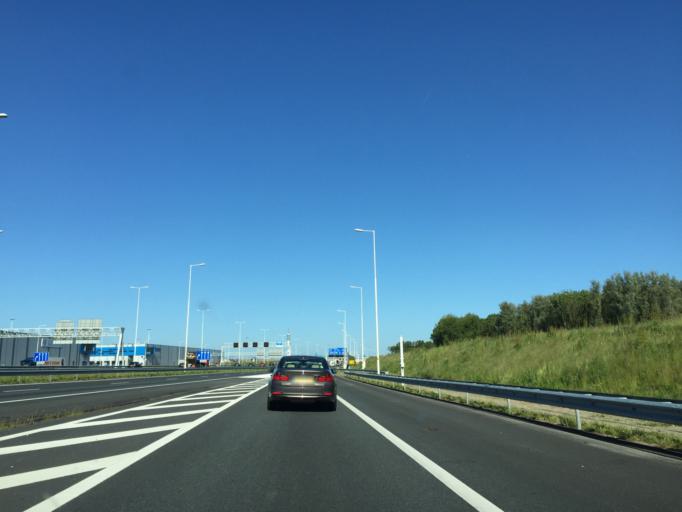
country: NL
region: South Holland
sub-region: Gemeente Albrandswaard
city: Rhoon
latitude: 51.8734
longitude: 4.4021
